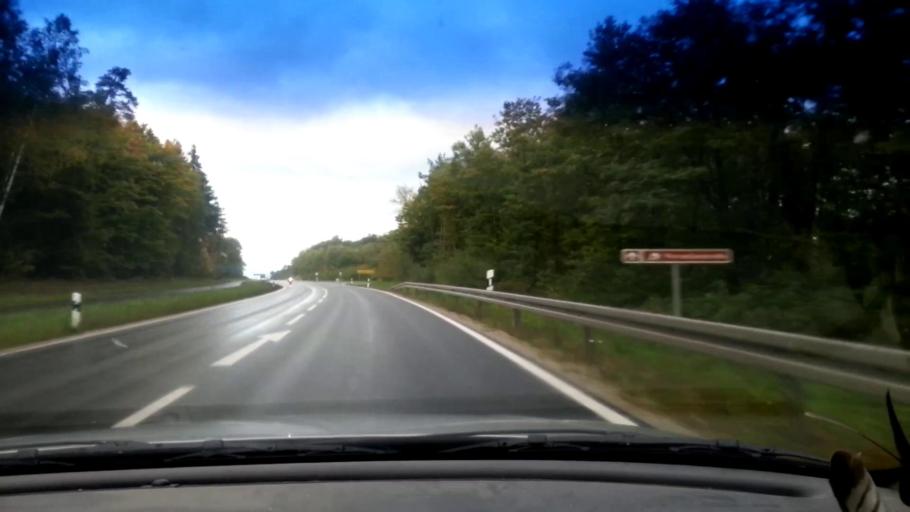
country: DE
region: Bavaria
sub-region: Upper Franconia
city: Burgebrach
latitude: 49.8069
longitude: 10.7313
